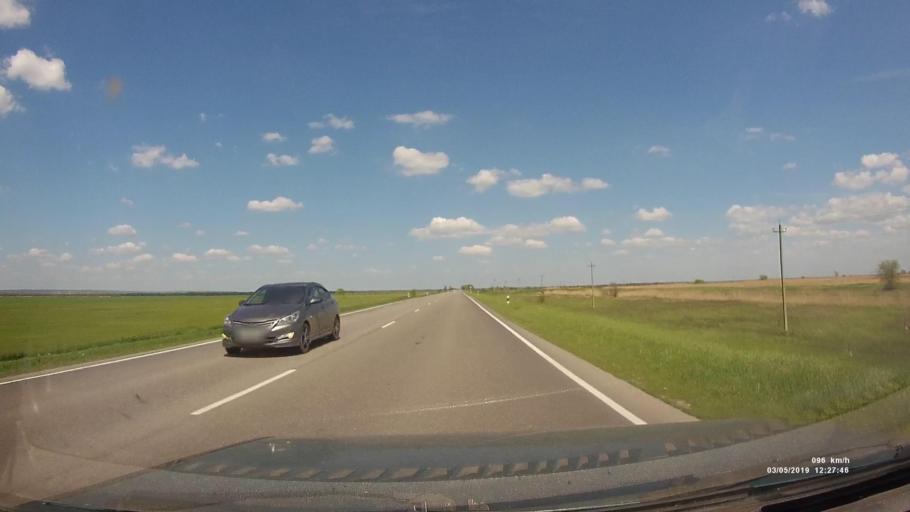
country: RU
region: Rostov
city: Semikarakorsk
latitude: 47.4634
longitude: 40.7230
